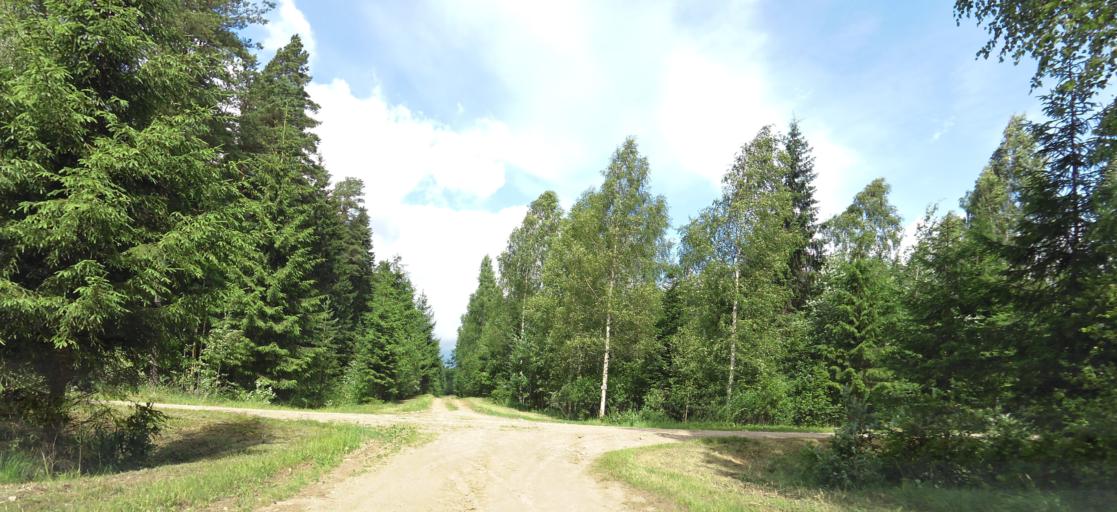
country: LT
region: Panevezys
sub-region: Birzai
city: Birzai
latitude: 56.2686
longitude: 24.7514
